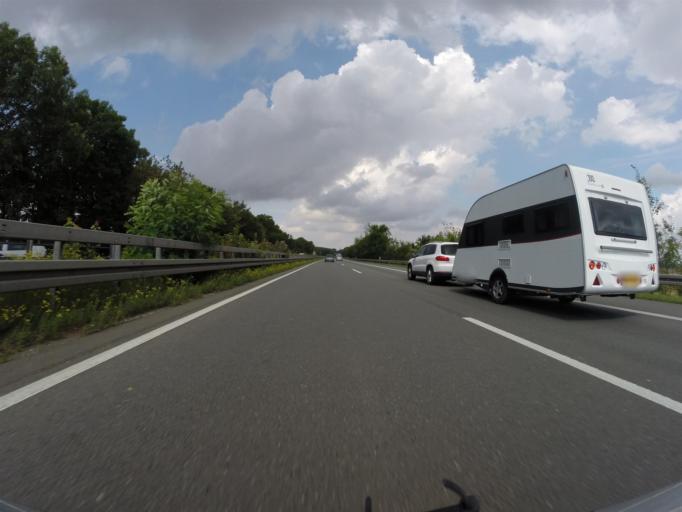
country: DE
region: North Rhine-Westphalia
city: Marsberg
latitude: 51.5421
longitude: 8.8335
